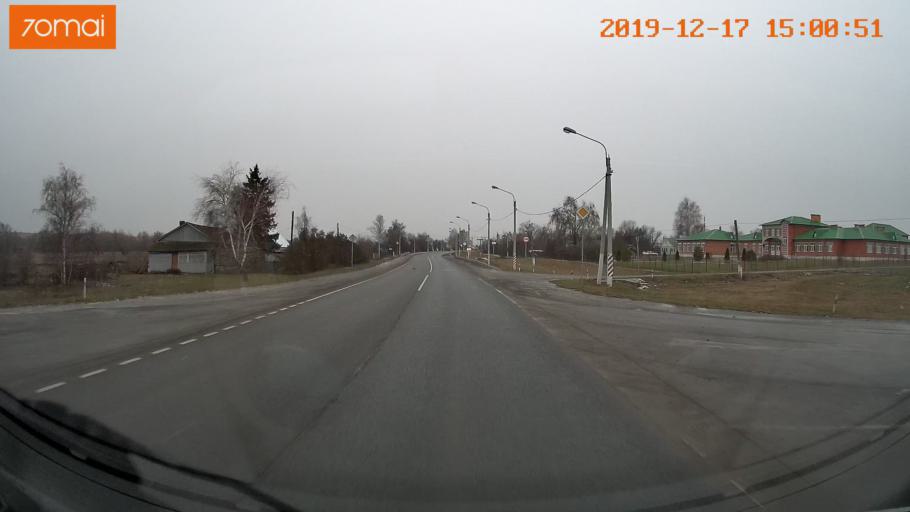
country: RU
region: Rjazan
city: Zakharovo
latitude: 54.2889
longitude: 39.1823
